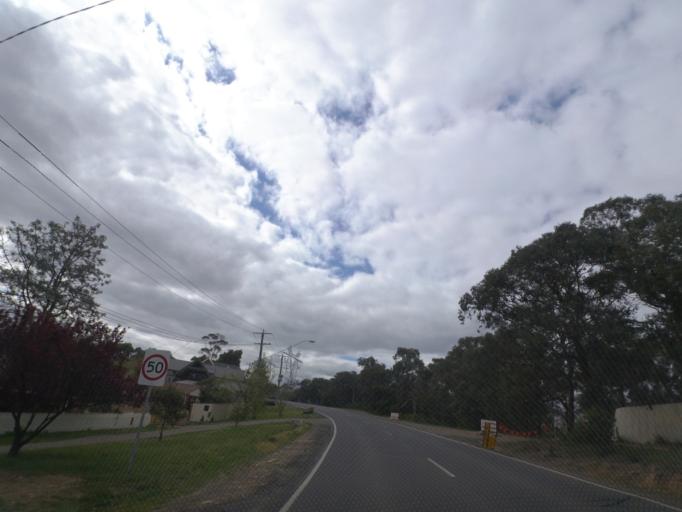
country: AU
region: Victoria
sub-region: Nillumbik
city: Diamond Creek
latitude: -37.6667
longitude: 145.1640
